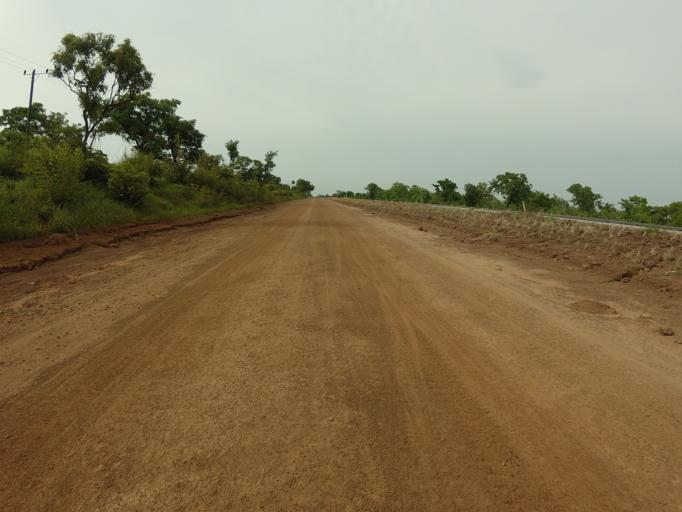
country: GH
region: Northern
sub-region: Yendi
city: Yendi
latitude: 9.6498
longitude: -0.0697
